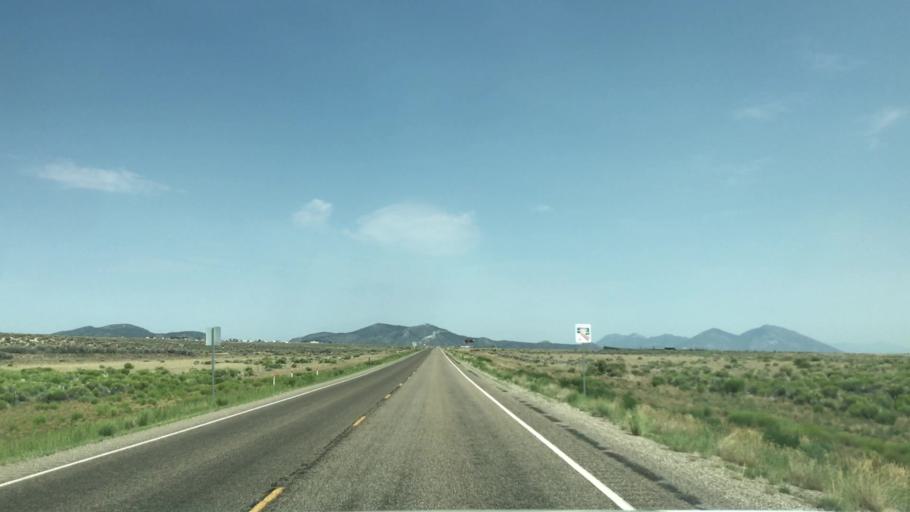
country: US
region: Nevada
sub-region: White Pine County
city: Ely
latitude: 39.1770
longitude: -114.8251
